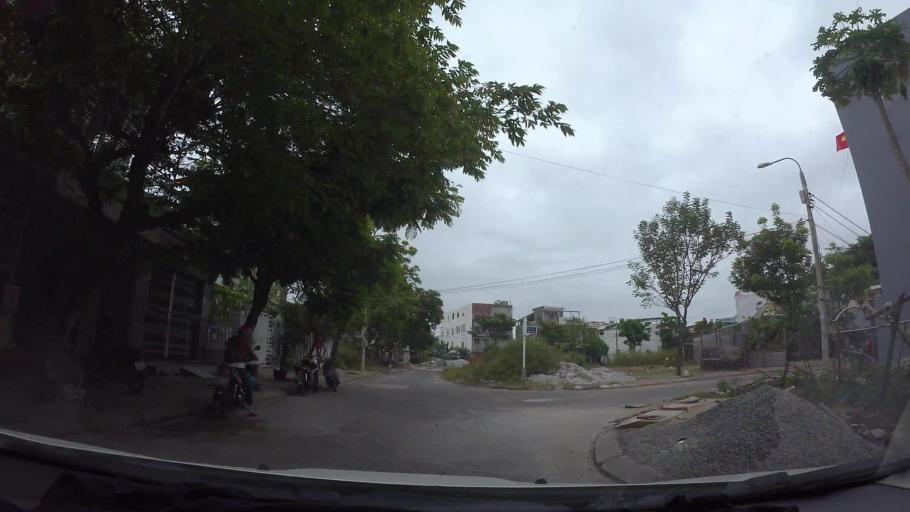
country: VN
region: Da Nang
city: Lien Chieu
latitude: 16.1250
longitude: 108.1189
